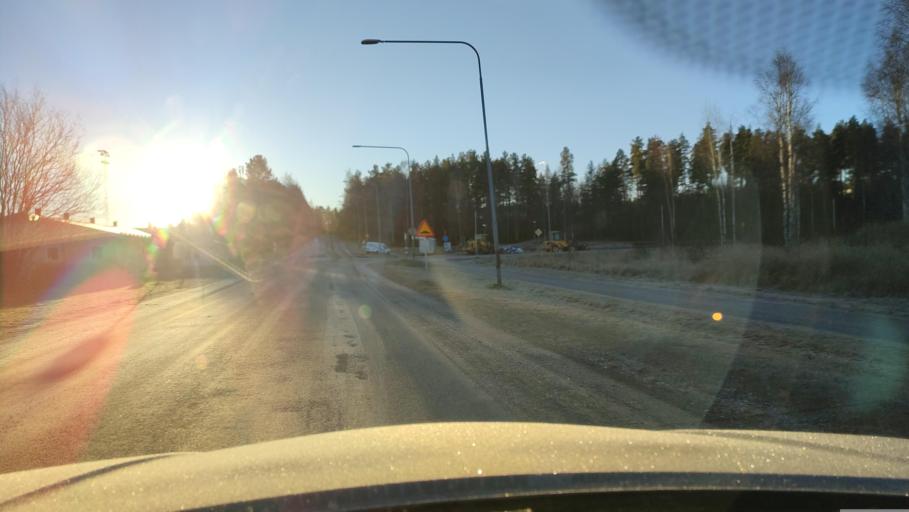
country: SE
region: Vaesterbotten
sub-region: Skelleftea Kommun
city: Skelleftea
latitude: 64.7406
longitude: 20.9423
